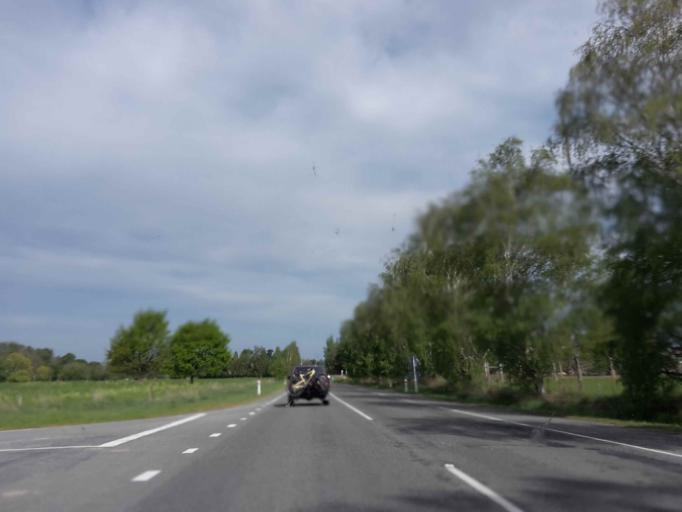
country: NZ
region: Canterbury
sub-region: Timaru District
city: Pleasant Point
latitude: -44.1134
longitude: 171.1706
